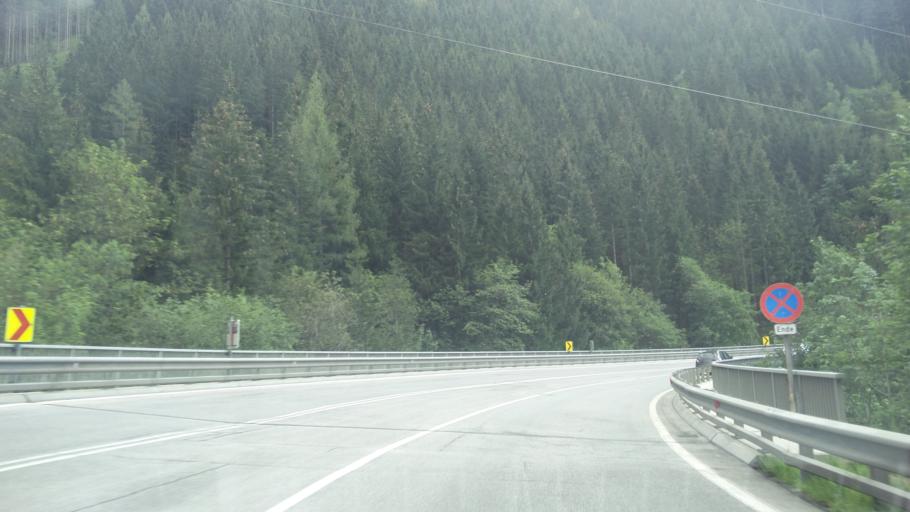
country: AT
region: Styria
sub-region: Politischer Bezirk Leoben
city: Eisenerz
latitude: 47.5500
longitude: 14.9360
